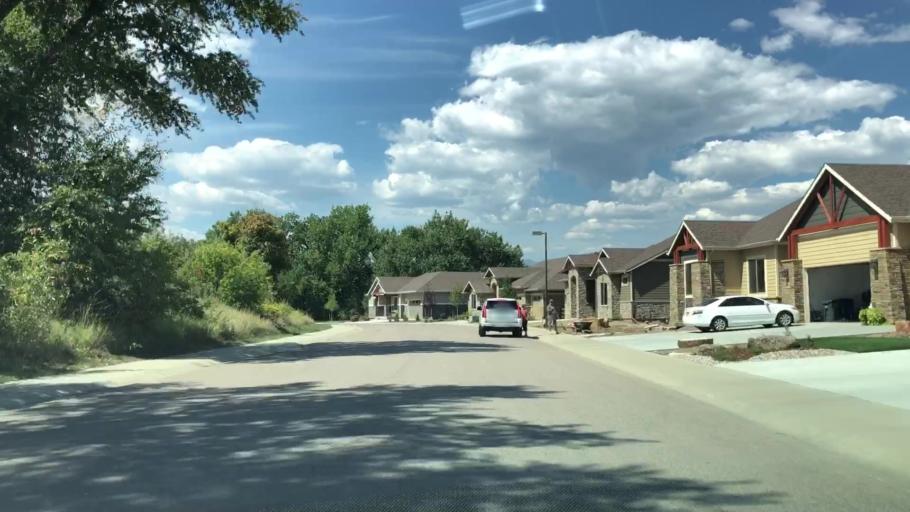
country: US
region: Colorado
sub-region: Larimer County
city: Loveland
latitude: 40.3961
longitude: -105.1522
